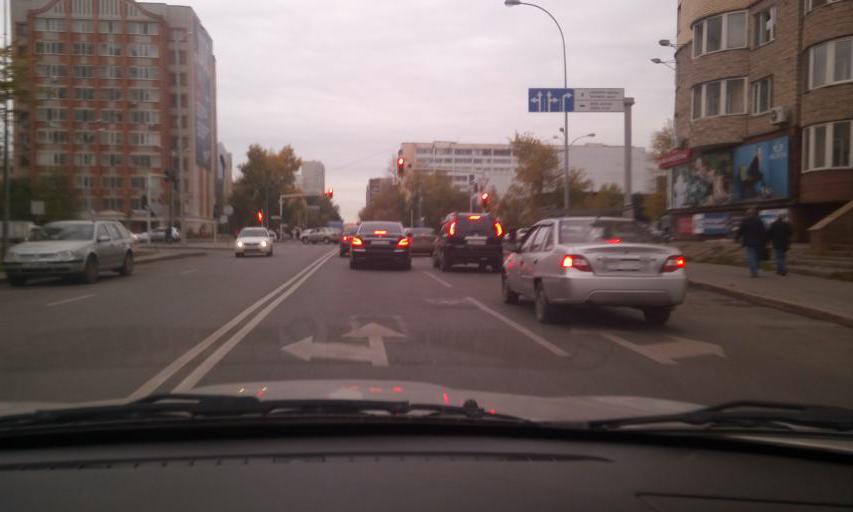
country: KZ
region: Astana Qalasy
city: Astana
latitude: 51.1731
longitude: 71.4131
